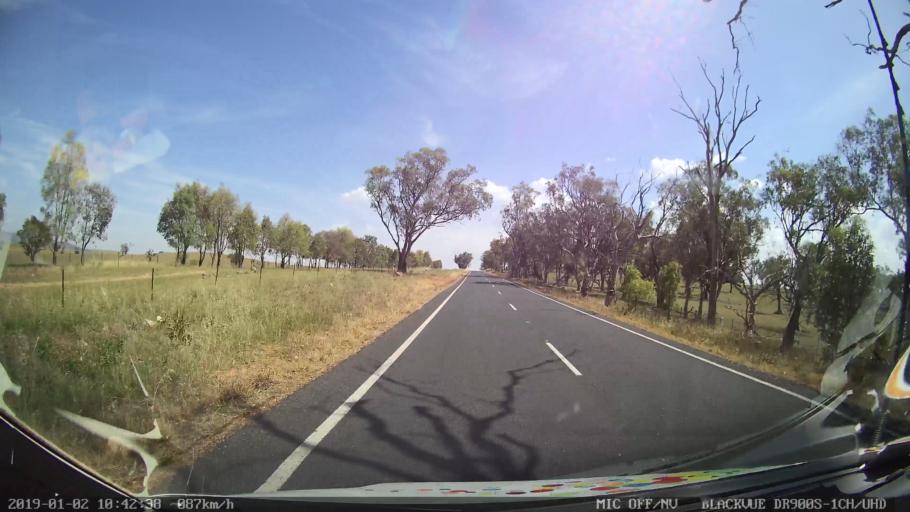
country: AU
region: New South Wales
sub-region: Cootamundra
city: Cootamundra
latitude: -34.7821
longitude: 148.3067
